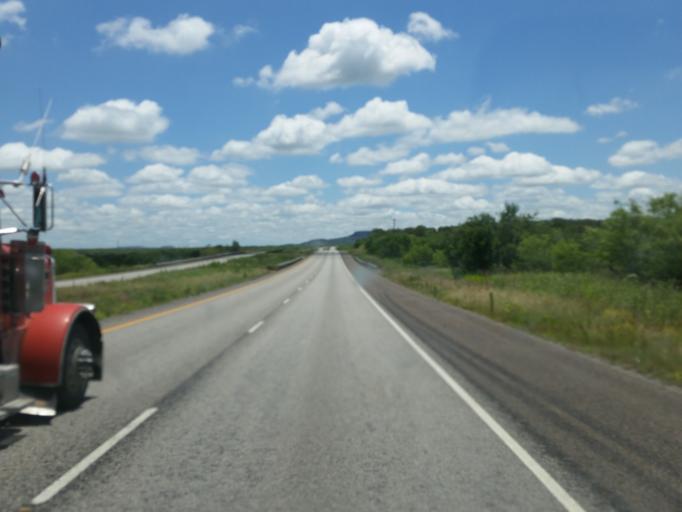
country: US
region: Texas
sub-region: Garza County
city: Post
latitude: 32.9844
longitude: -101.1243
